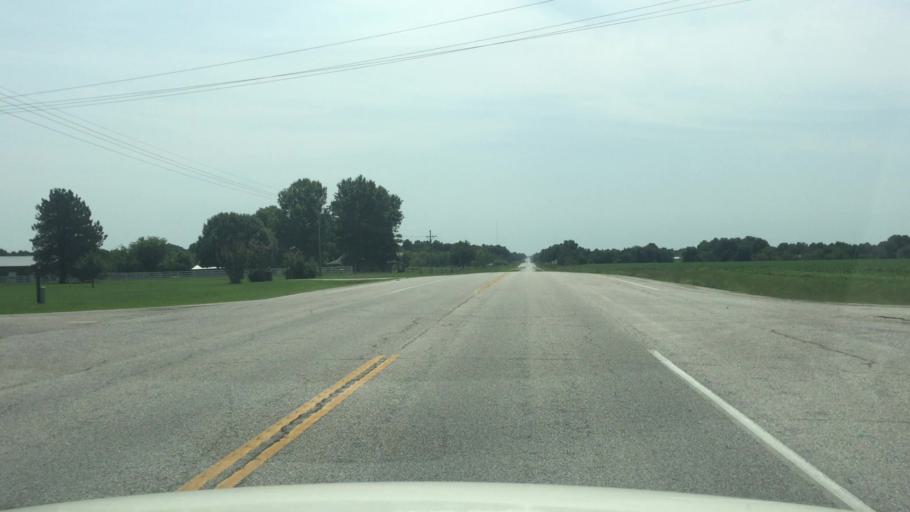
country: US
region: Kansas
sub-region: Cherokee County
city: Galena
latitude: 37.1486
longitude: -94.7043
